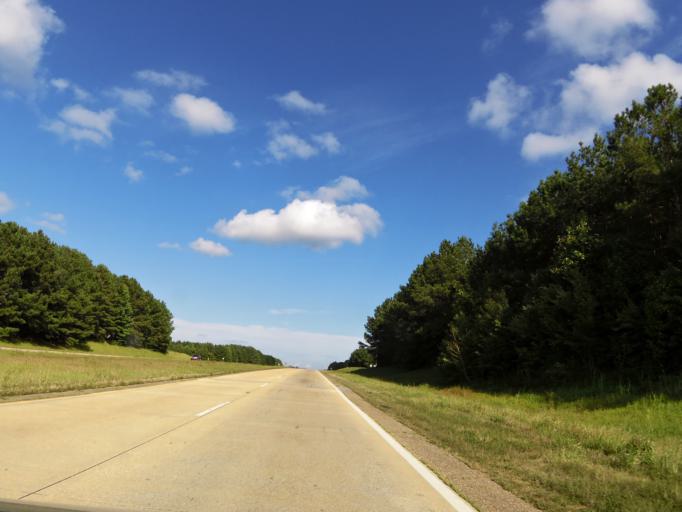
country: US
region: Mississippi
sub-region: Tishomingo County
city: Iuka
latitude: 34.8083
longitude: -88.2724
